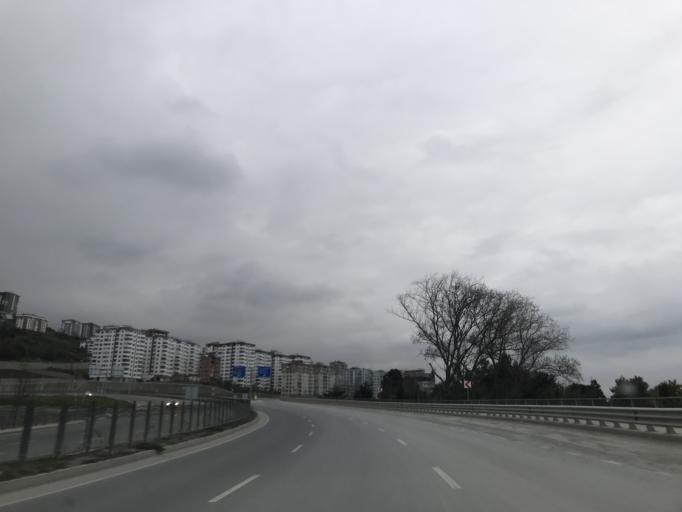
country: TR
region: Trabzon
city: Akcaabat
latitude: 41.0067
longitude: 39.6308
